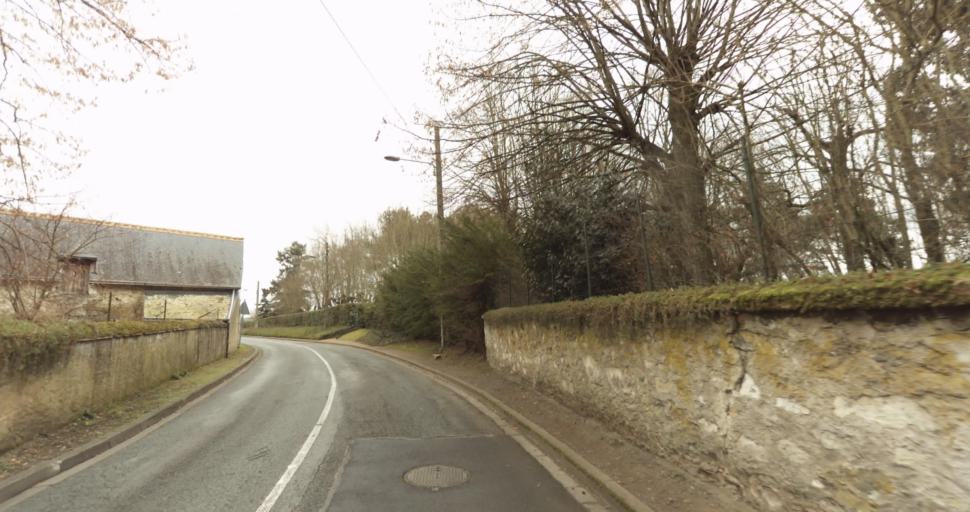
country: FR
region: Pays de la Loire
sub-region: Departement de Maine-et-Loire
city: Jumelles
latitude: 47.3769
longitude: -0.1160
